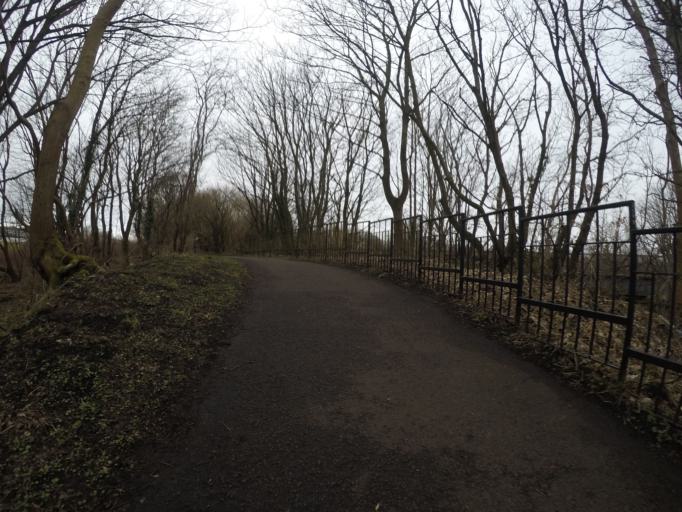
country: GB
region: Scotland
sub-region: North Ayrshire
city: Kilwinning
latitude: 55.6448
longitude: -4.6901
